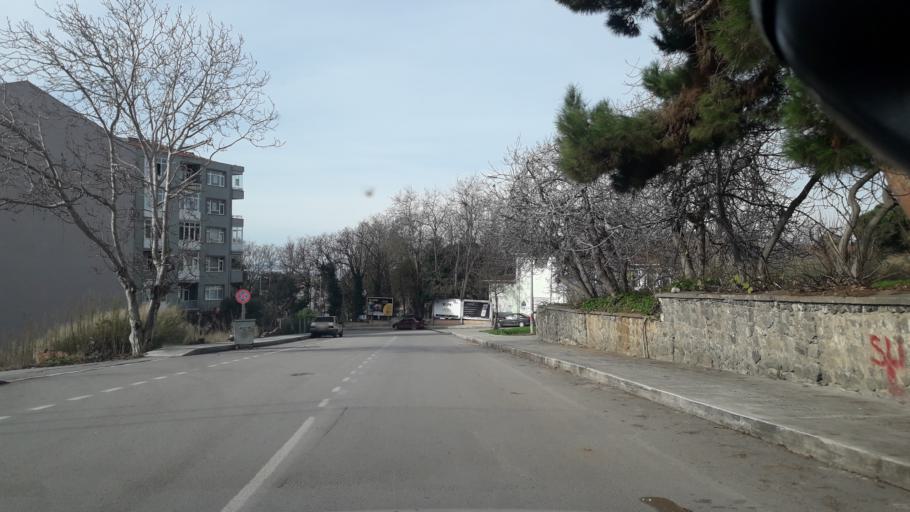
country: TR
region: Sinop
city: Sinop
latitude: 42.0288
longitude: 35.1574
